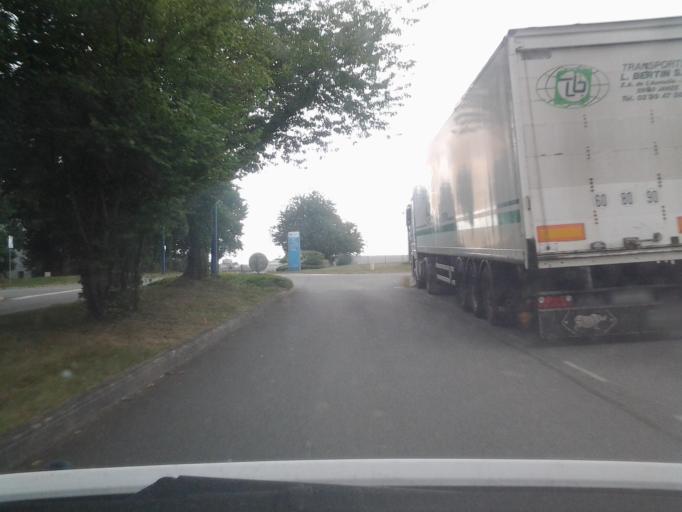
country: FR
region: Pays de la Loire
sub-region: Departement de la Vendee
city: La Roche-sur-Yon
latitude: 46.6938
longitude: -1.4260
